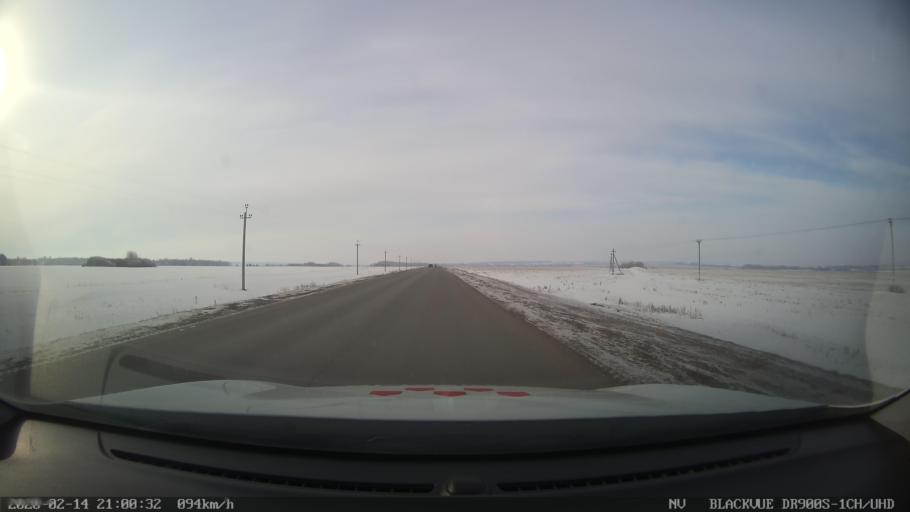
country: RU
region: Tatarstan
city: Kuybyshevskiy Zaton
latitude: 55.1703
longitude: 49.2177
